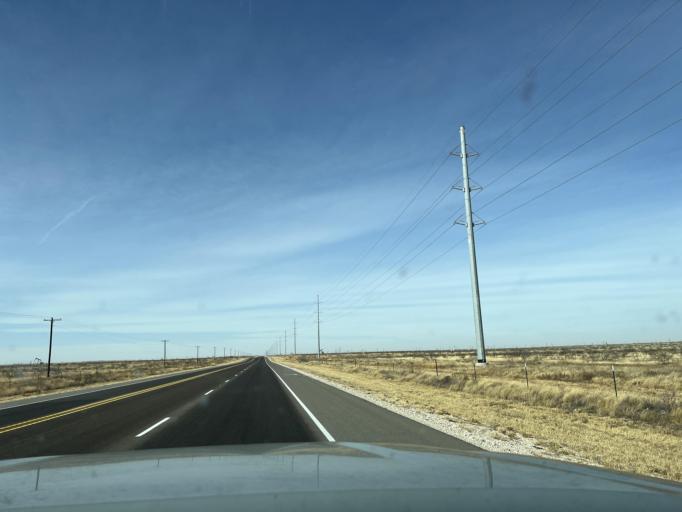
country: US
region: Texas
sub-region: Andrews County
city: Andrews
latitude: 32.3452
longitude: -102.7103
